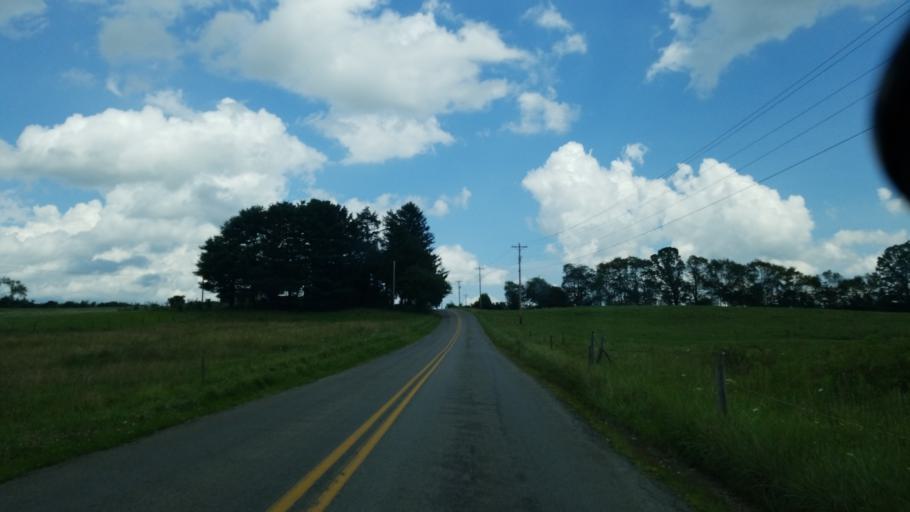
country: US
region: Pennsylvania
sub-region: Jefferson County
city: Brookville
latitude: 41.2391
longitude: -79.0314
